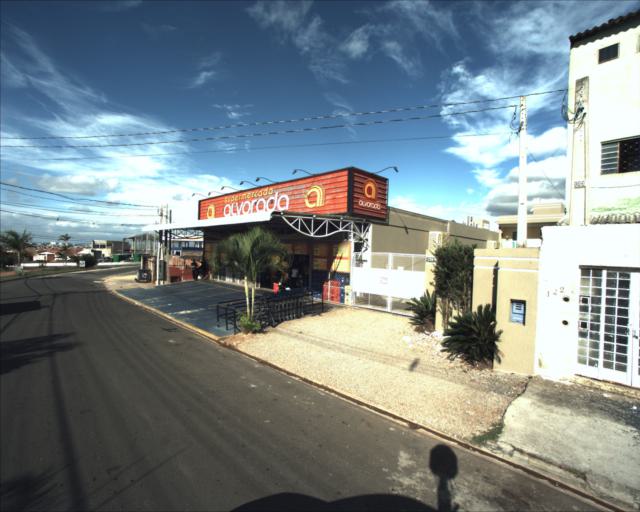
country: BR
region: Sao Paulo
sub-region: Sorocaba
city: Sorocaba
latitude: -23.5105
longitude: -47.5161
